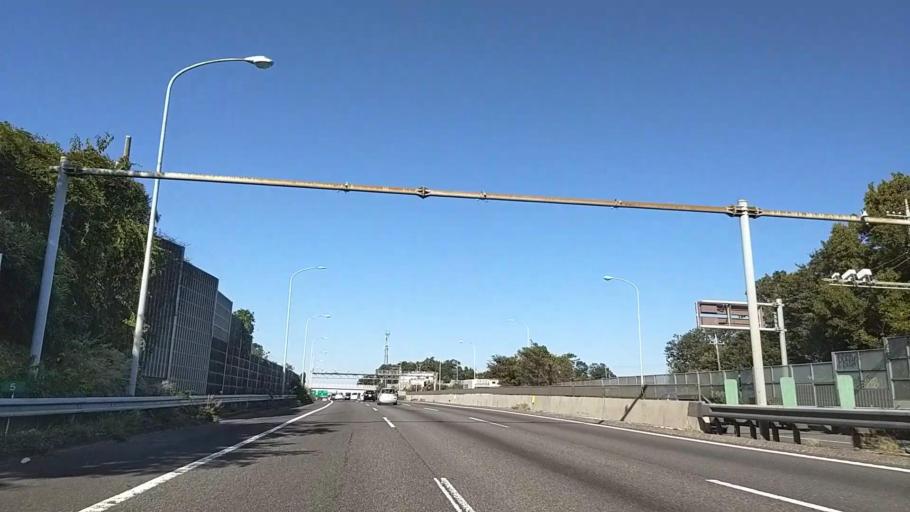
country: JP
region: Kanagawa
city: Minami-rinkan
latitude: 35.4771
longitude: 139.5252
